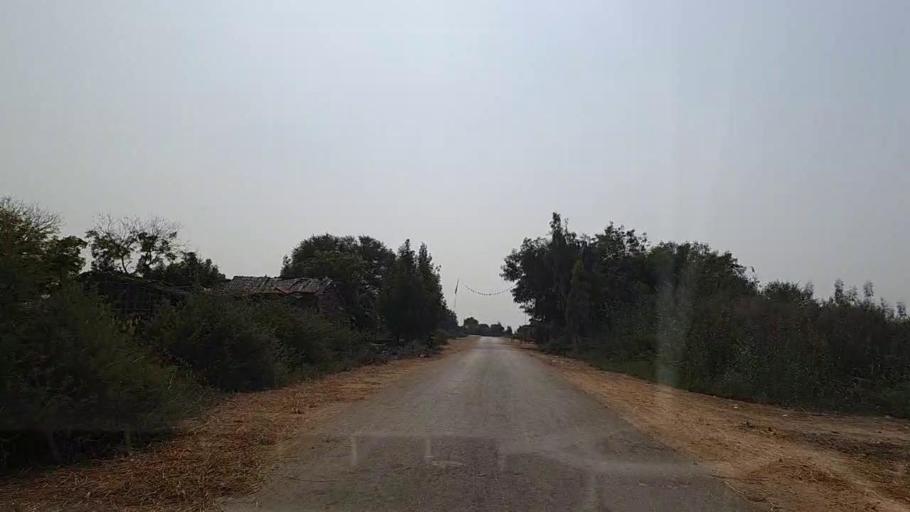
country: PK
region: Sindh
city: Chuhar Jamali
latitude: 24.2493
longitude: 67.9053
